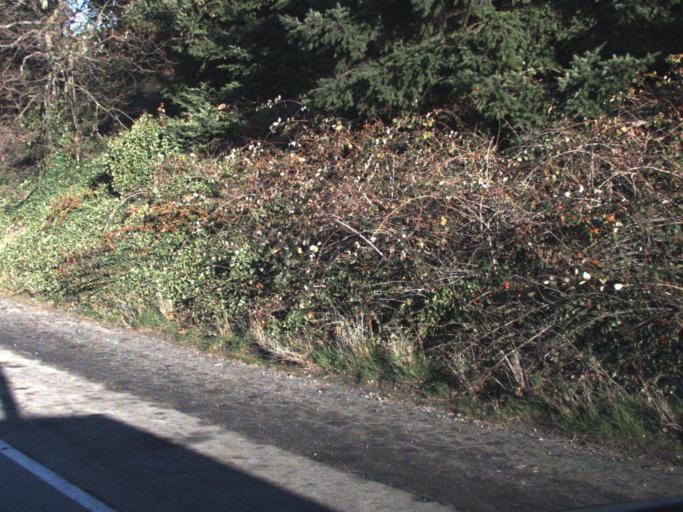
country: US
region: Washington
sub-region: King County
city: Boulevard Park
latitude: 47.5408
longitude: -122.3023
